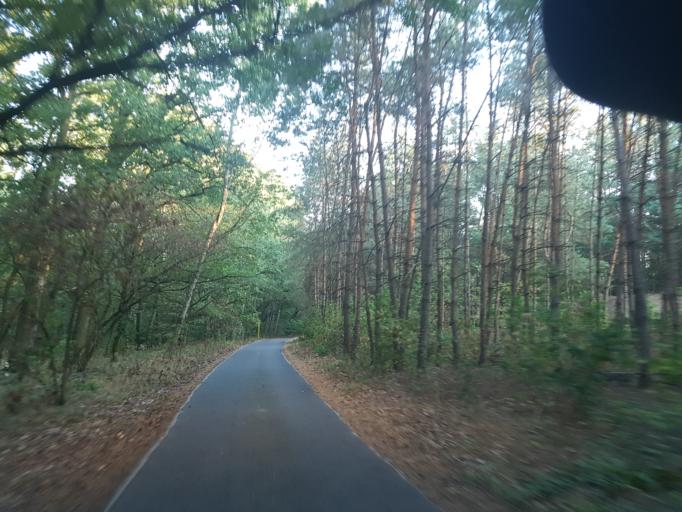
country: DE
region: Brandenburg
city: Herzberg
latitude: 51.6510
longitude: 13.2849
